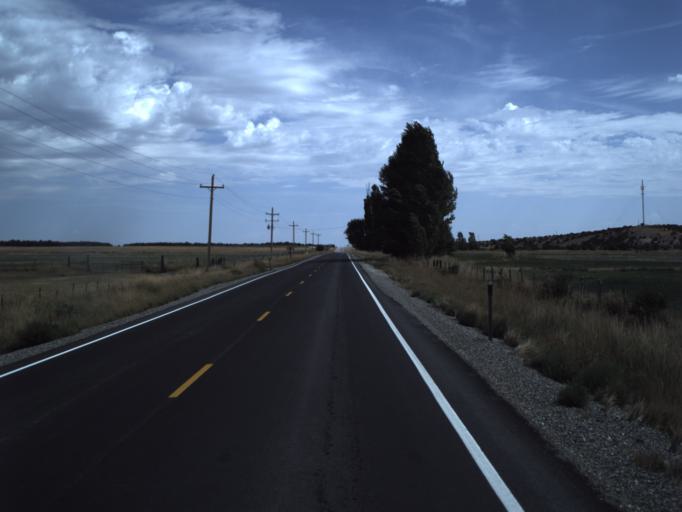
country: US
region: Idaho
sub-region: Cassia County
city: Burley
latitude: 41.8170
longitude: -113.3163
